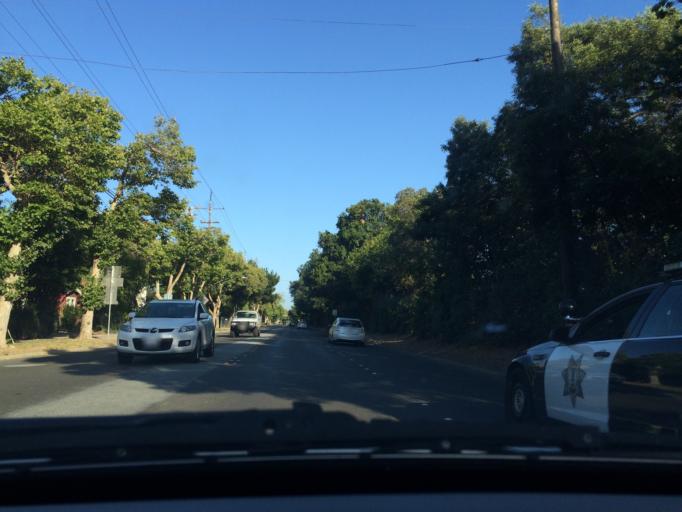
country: US
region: California
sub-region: Santa Clara County
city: Palo Alto
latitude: 37.4380
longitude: -122.1554
